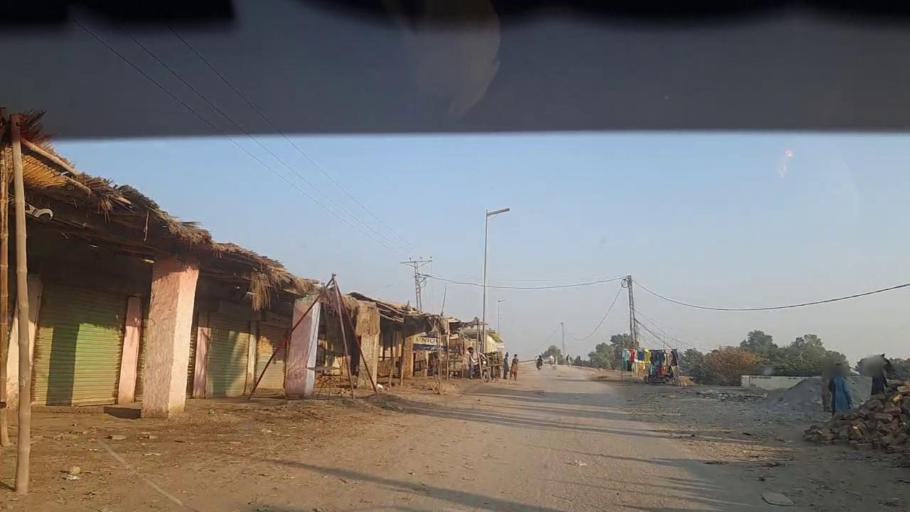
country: PK
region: Sindh
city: Ranipur
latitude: 27.2843
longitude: 68.5113
